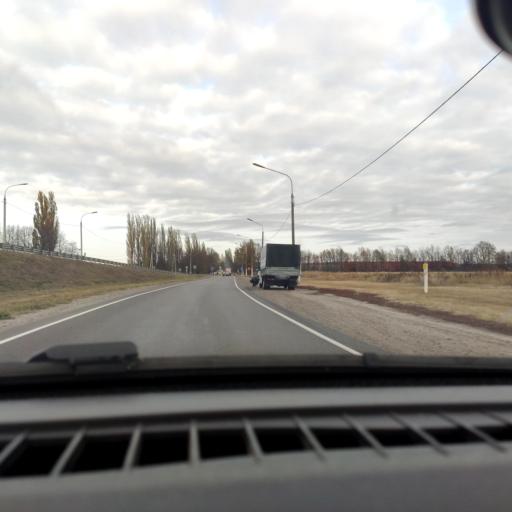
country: RU
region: Voronezj
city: Podgornoye
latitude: 51.7995
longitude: 39.2040
